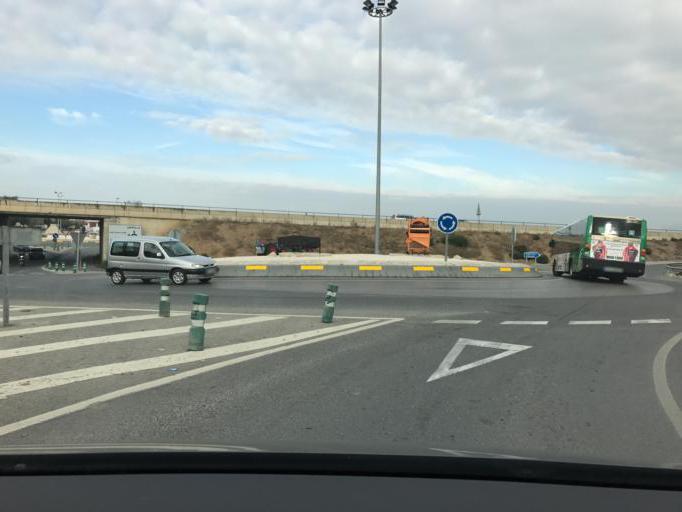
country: ES
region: Andalusia
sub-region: Provincia de Granada
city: Ogijares
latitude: 37.1223
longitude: -3.6157
